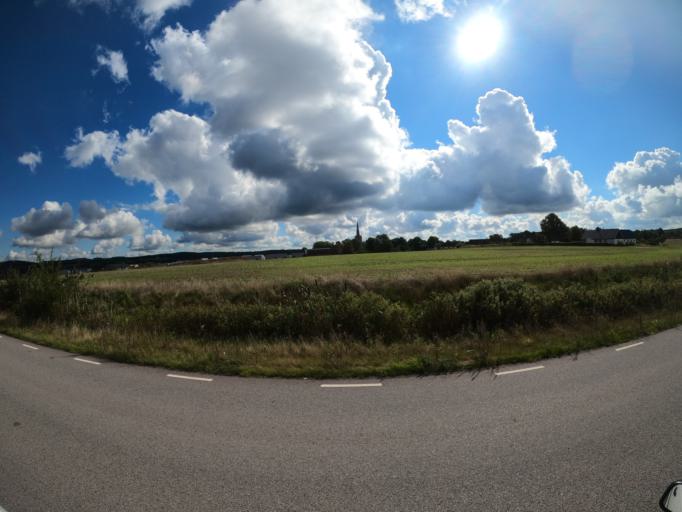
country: SE
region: Skane
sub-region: Lunds Kommun
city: Genarp
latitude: 55.6049
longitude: 13.3899
